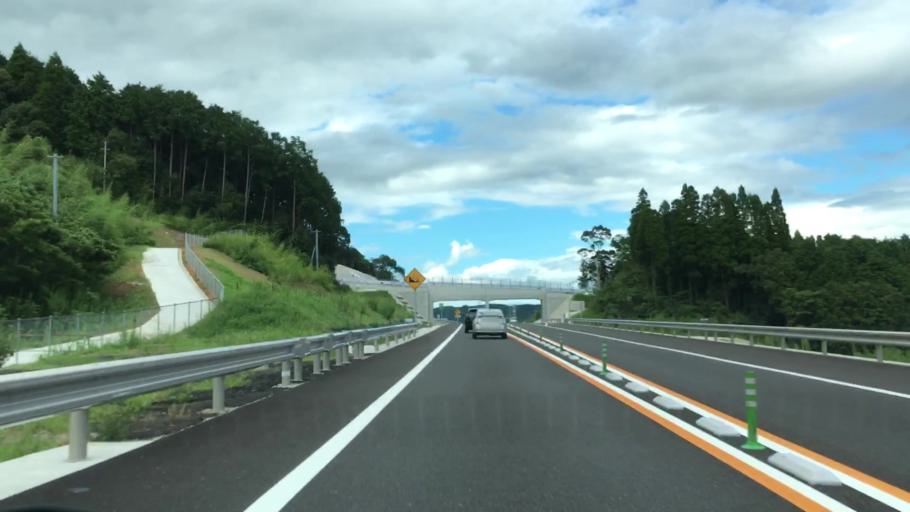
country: JP
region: Saga Prefecture
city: Imaricho-ko
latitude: 33.3302
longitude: 129.9279
